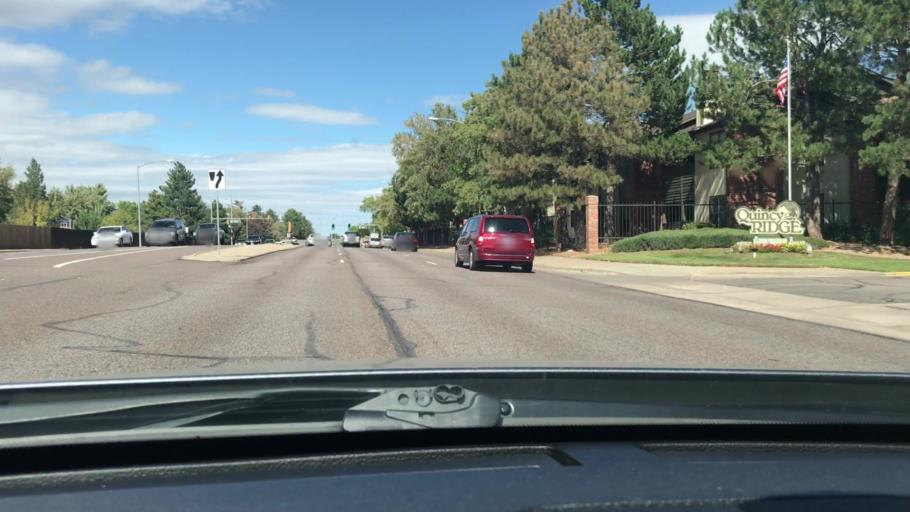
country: US
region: Colorado
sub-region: Arapahoe County
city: Dove Valley
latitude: 39.6369
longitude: -104.8102
